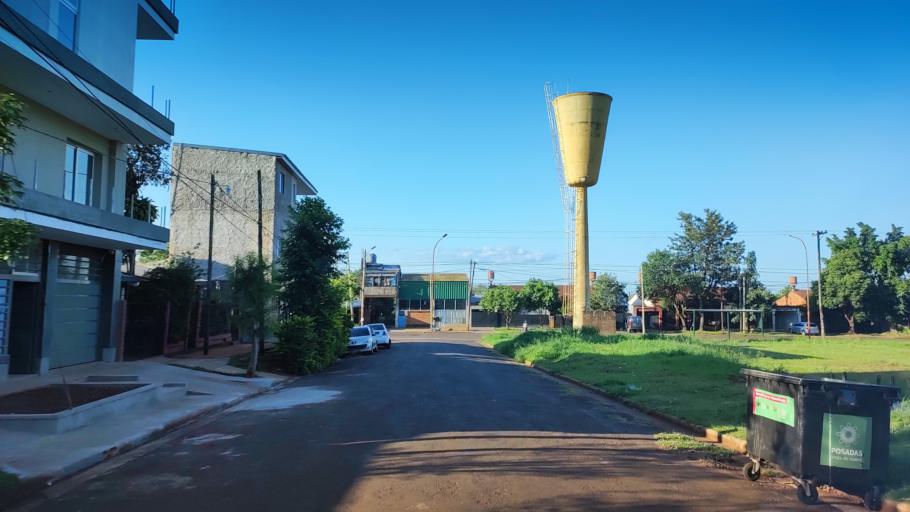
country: AR
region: Misiones
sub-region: Departamento de Capital
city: Posadas
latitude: -27.3701
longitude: -55.9425
